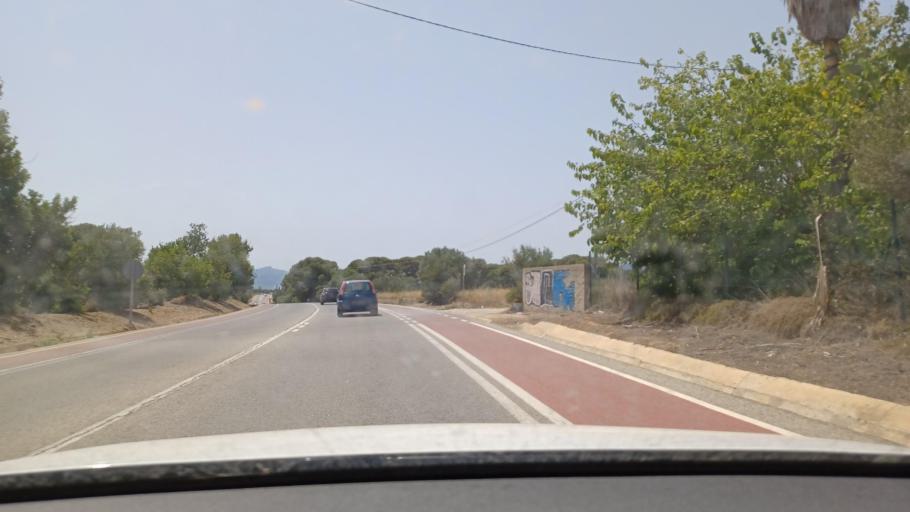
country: ES
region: Catalonia
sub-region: Provincia de Tarragona
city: Cambrils
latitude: 41.0680
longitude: 1.0394
